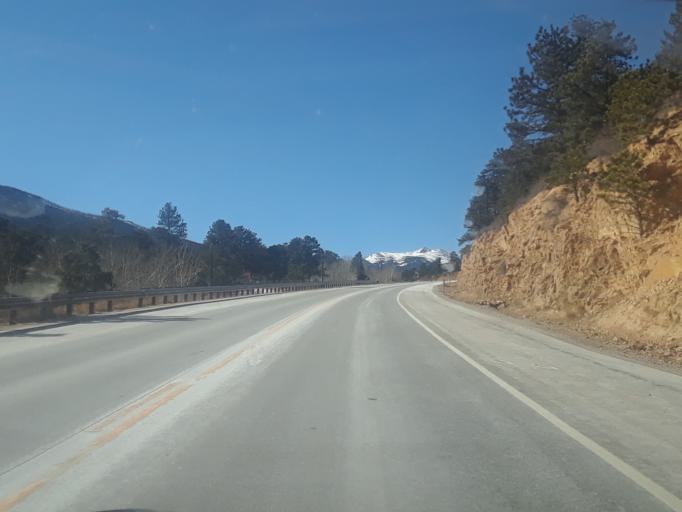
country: US
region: Colorado
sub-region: Larimer County
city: Estes Park
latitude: 40.1945
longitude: -105.5205
